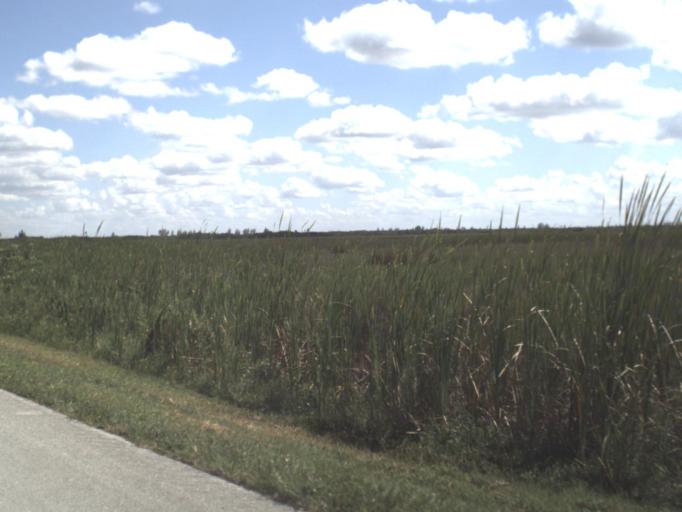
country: US
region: Florida
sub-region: Collier County
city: Marco
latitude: 25.9181
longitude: -81.3869
